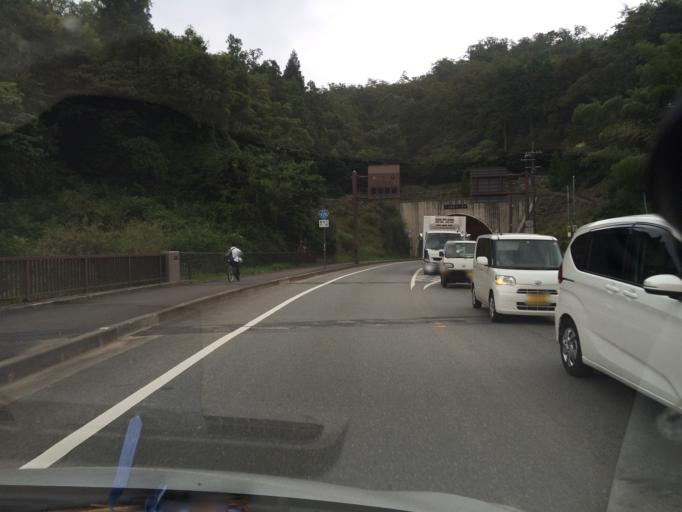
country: JP
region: Hyogo
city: Toyooka
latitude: 35.5262
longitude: 134.8091
